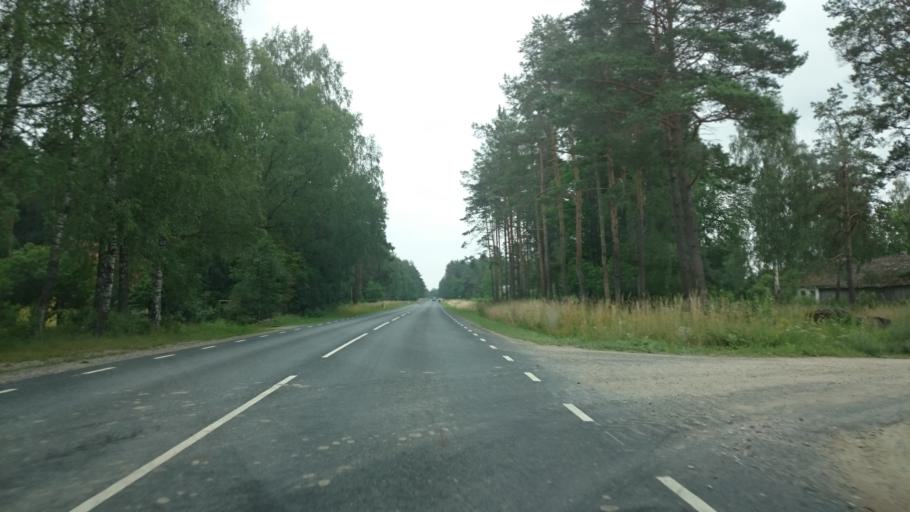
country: EE
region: Saare
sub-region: Orissaare vald
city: Orissaare
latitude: 58.5990
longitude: 23.3210
